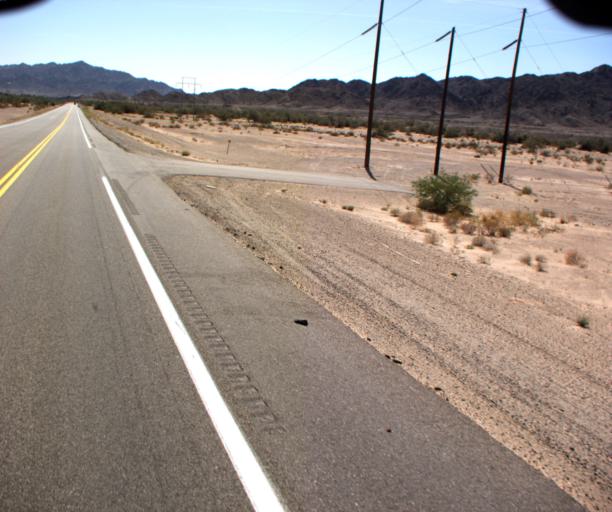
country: US
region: Arizona
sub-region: Yuma County
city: Fortuna Foothills
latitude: 32.8050
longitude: -114.3803
